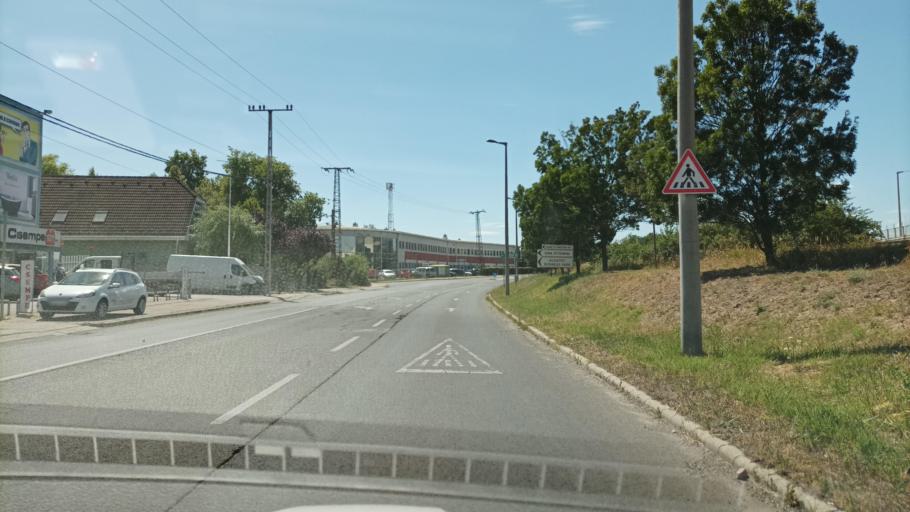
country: HU
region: Pest
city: Budaors
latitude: 47.4487
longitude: 18.9656
